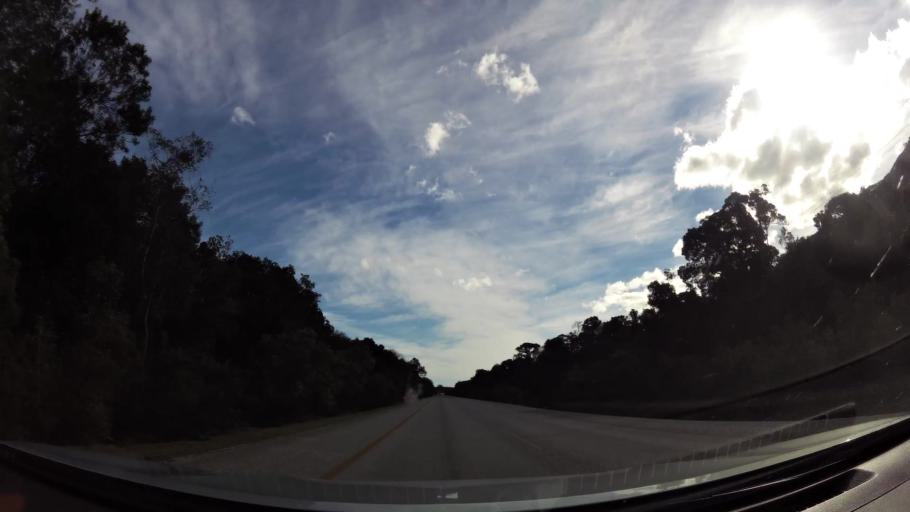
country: ZA
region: Eastern Cape
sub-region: Cacadu District Municipality
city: Kareedouw
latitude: -33.9910
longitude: 24.1010
